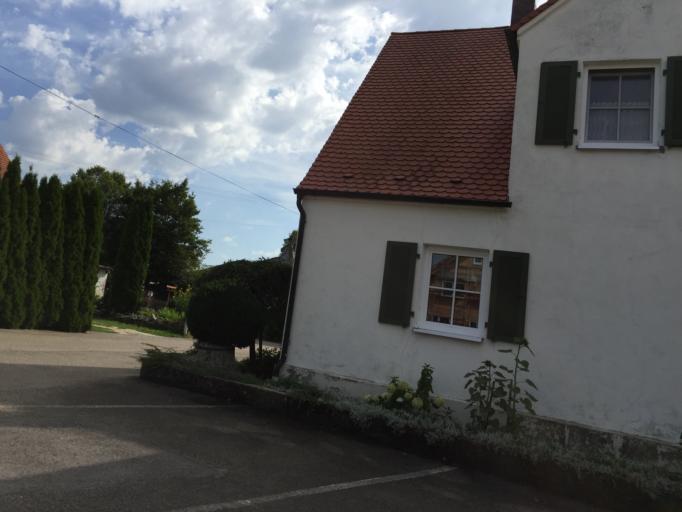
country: DE
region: Baden-Wuerttemberg
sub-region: Regierungsbezirk Stuttgart
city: Kirchheim am Ries
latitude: 48.8417
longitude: 10.4050
